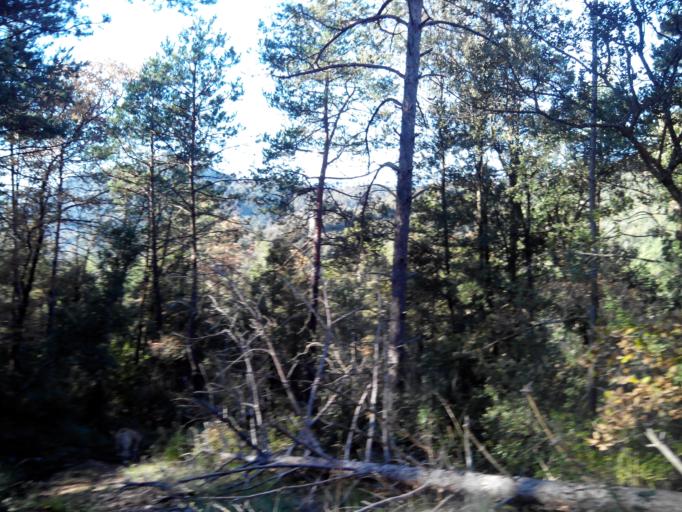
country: ES
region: Catalonia
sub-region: Provincia de Barcelona
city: Vilada
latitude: 42.1065
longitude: 1.9343
